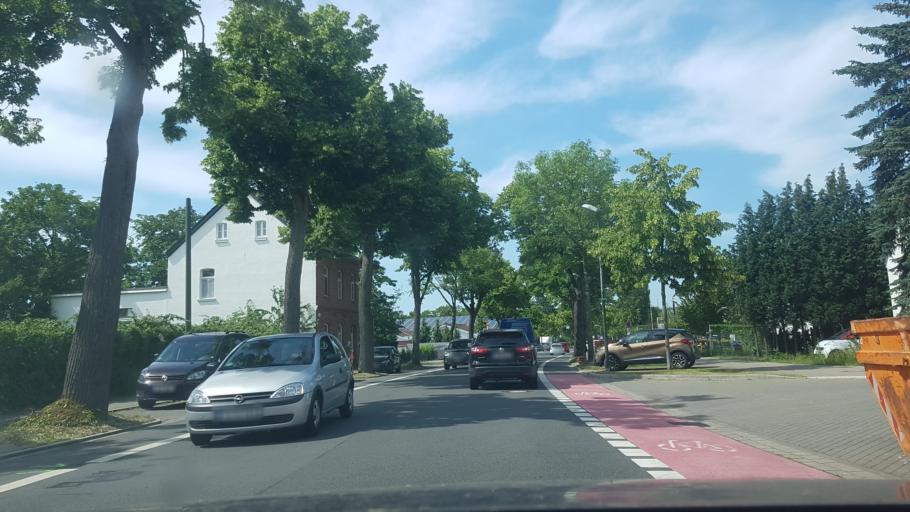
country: DE
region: North Rhine-Westphalia
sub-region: Regierungsbezirk Dusseldorf
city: Dusseldorf
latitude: 51.2785
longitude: 6.7414
